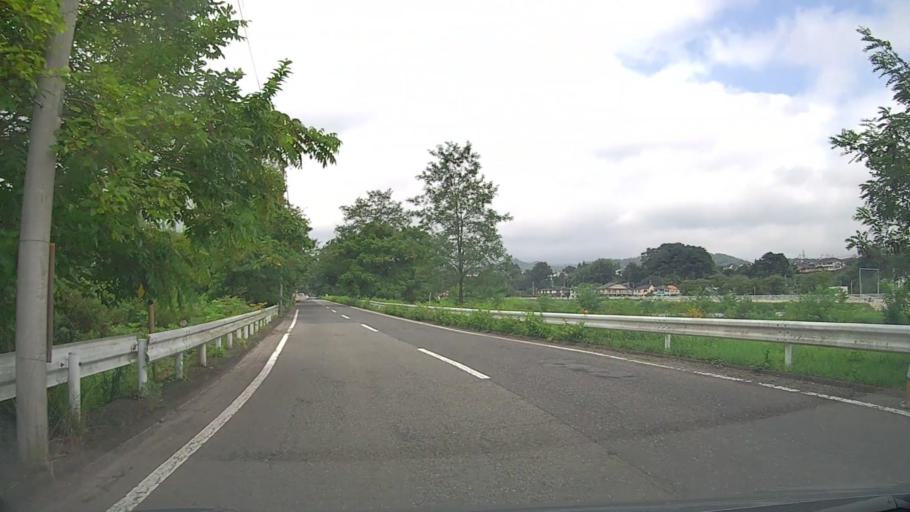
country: JP
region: Tokyo
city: Itsukaichi
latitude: 35.7219
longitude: 139.2617
